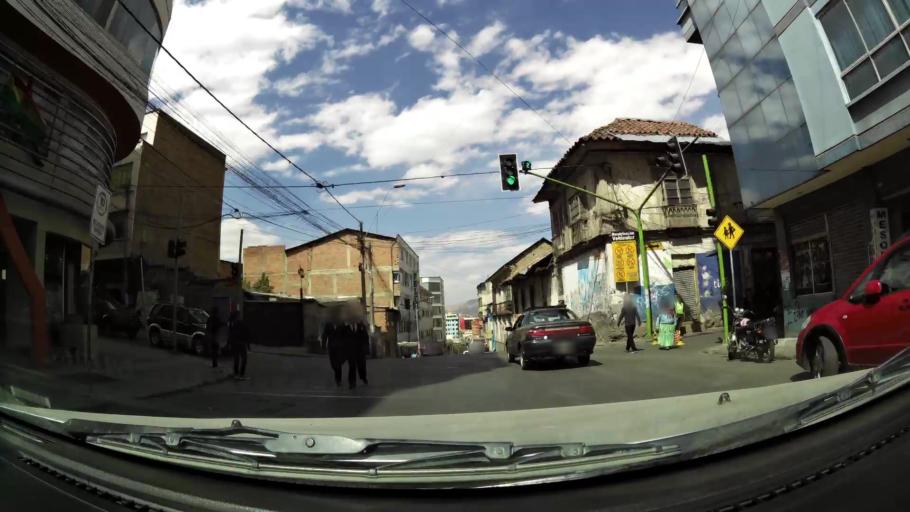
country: BO
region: La Paz
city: La Paz
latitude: -16.4937
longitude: -68.1328
